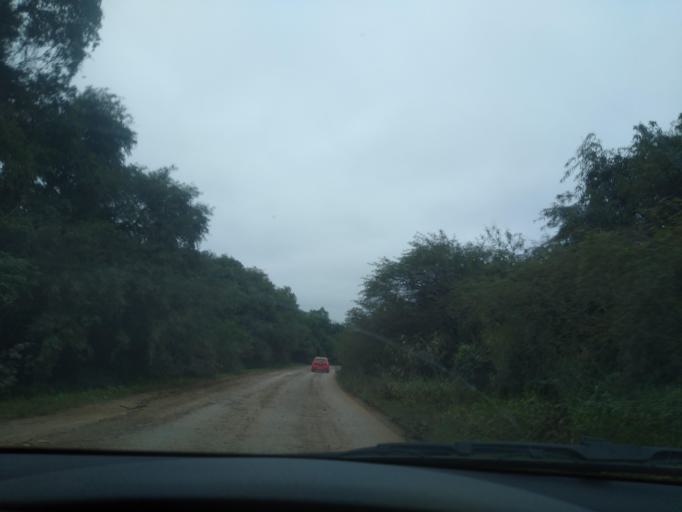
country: AR
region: Chaco
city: Colonia Benitez
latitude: -27.3364
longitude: -58.9676
